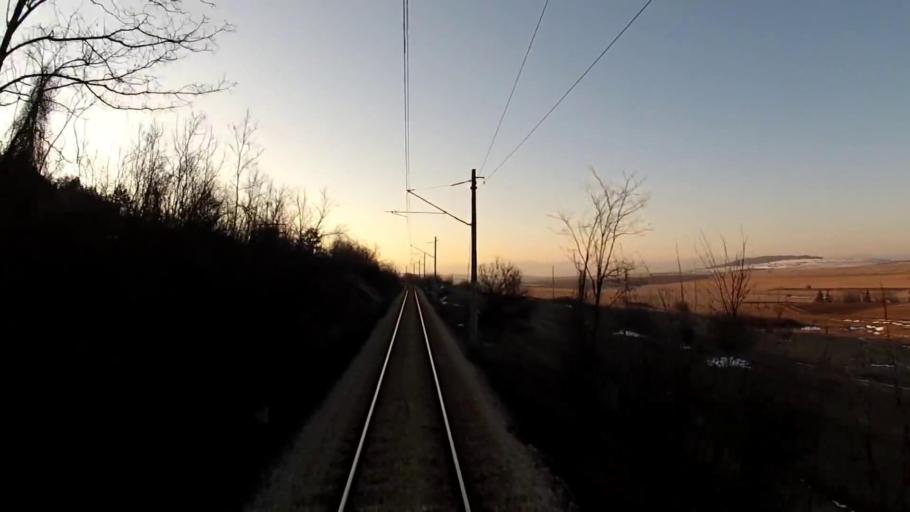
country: BG
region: Sofiya
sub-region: Obshtina Dragoman
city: Dragoman
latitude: 42.9005
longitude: 22.9512
